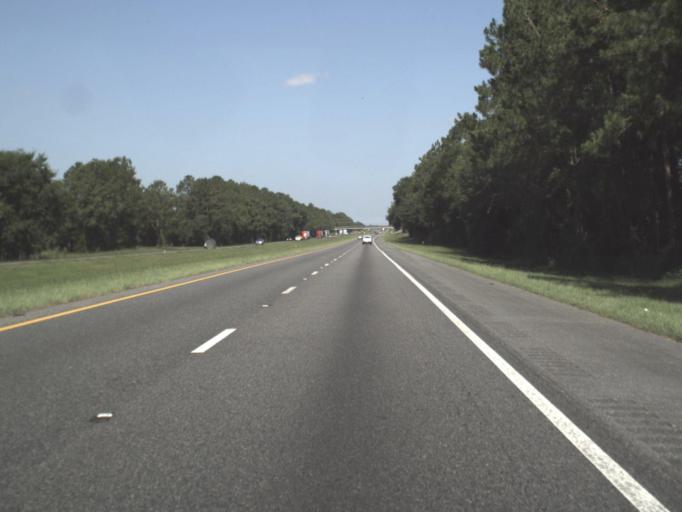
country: US
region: Florida
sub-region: Suwannee County
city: Live Oak
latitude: 30.3409
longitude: -83.1219
